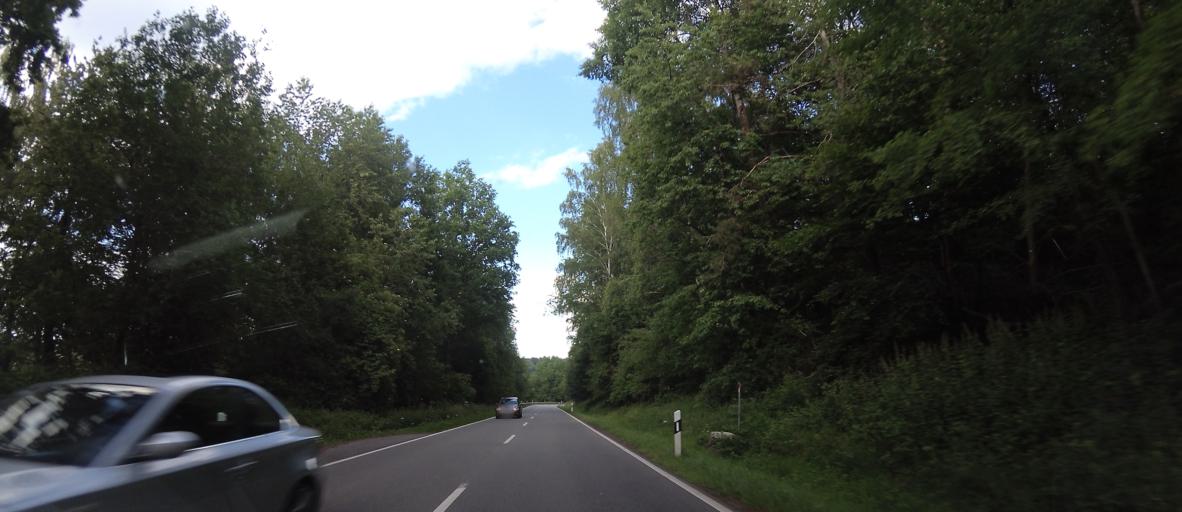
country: DE
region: Rheinland-Pfalz
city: Obersimten
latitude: 49.1717
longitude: 7.5812
